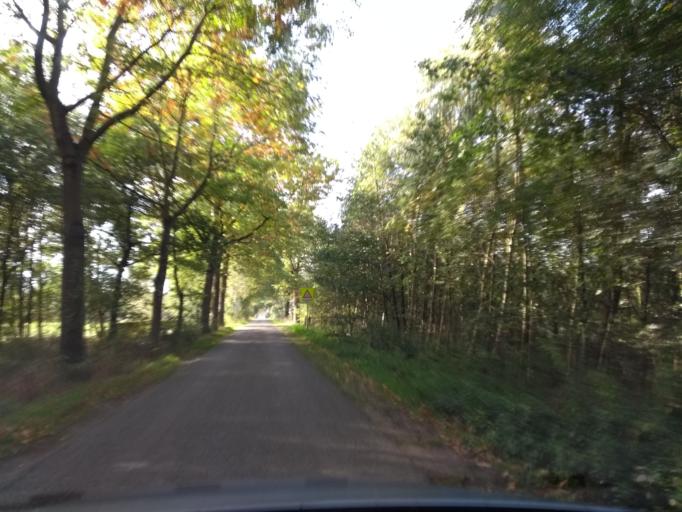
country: NL
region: Gelderland
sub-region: Gemeente Bronckhorst
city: Zelhem
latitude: 52.0626
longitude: 6.3849
